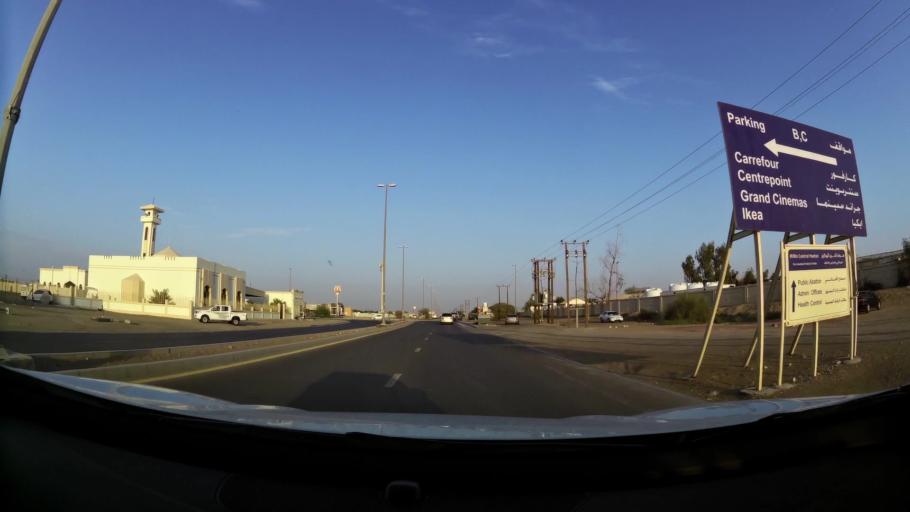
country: AE
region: Abu Dhabi
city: Al Ain
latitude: 24.1584
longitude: 55.8100
